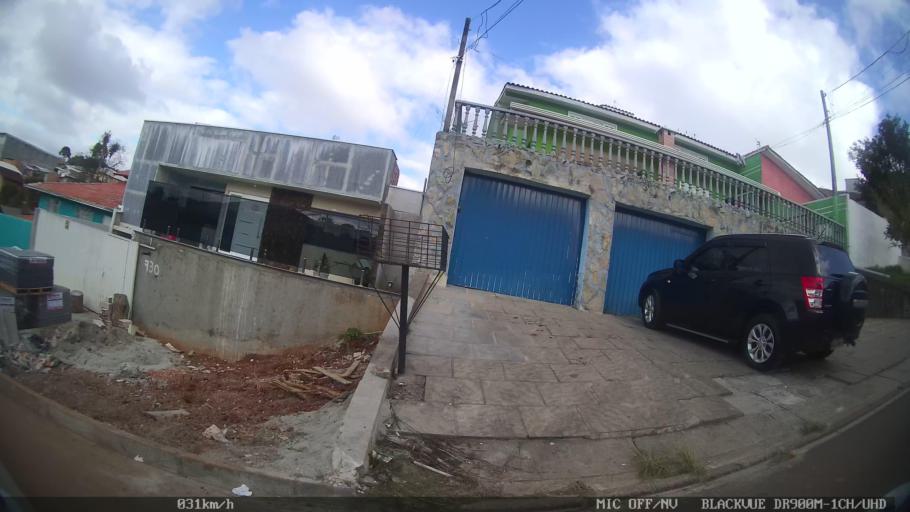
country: BR
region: Parana
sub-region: Colombo
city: Colombo
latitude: -25.3596
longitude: -49.1899
